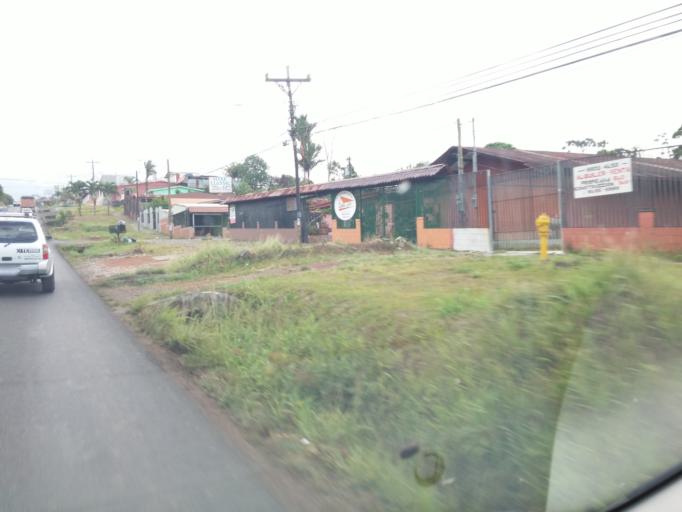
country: CR
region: Alajuela
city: Pital
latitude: 10.3903
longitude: -84.3388
